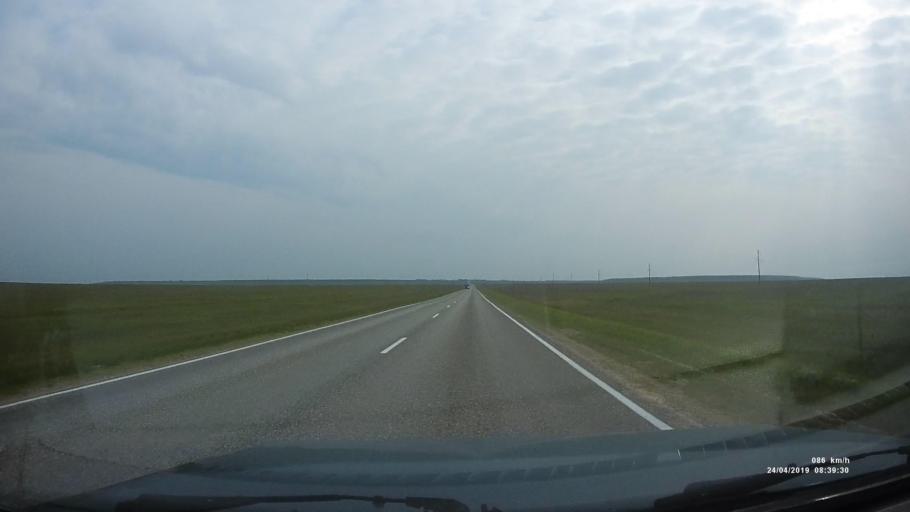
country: RU
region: Kalmykiya
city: Arshan'
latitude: 46.2213
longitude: 43.9852
